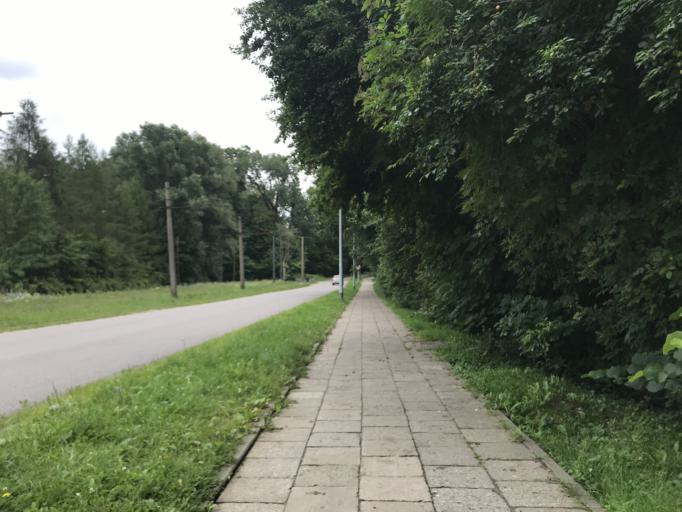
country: PL
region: Warmian-Masurian Voivodeship
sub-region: Powiat elblaski
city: Elblag
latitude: 54.1760
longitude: 19.4347
